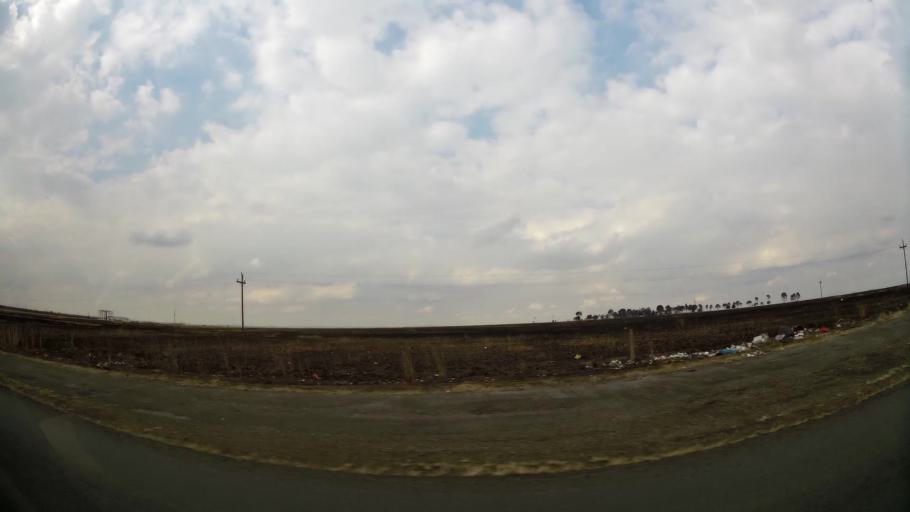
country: ZA
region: Orange Free State
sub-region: Fezile Dabi District Municipality
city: Sasolburg
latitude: -26.8719
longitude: 27.8873
